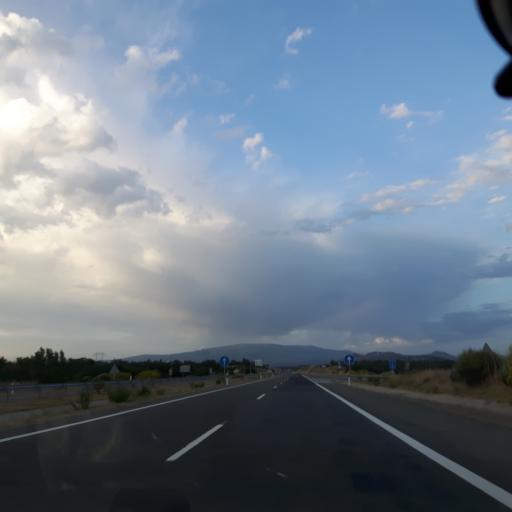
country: ES
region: Castille and Leon
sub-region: Provincia de Salamanca
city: Fuentes de Bejar
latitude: 40.5226
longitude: -5.6720
